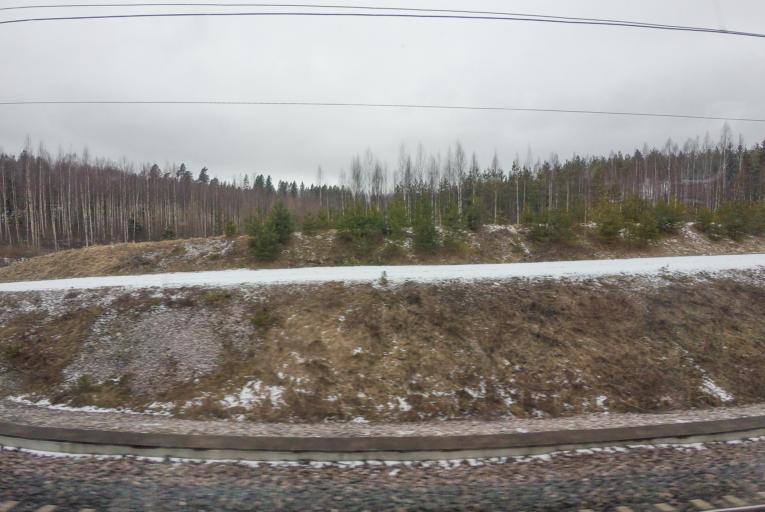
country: FI
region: Uusimaa
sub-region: Helsinki
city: Jaervenpaeae
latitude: 60.4509
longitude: 25.1234
